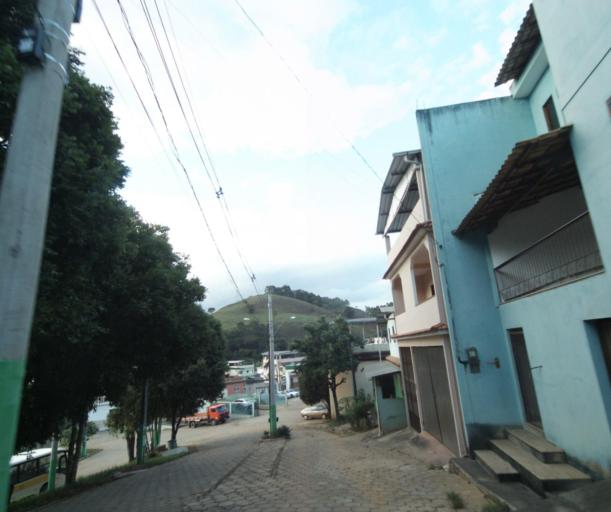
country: BR
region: Espirito Santo
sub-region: Guacui
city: Guacui
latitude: -20.6201
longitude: -41.6826
